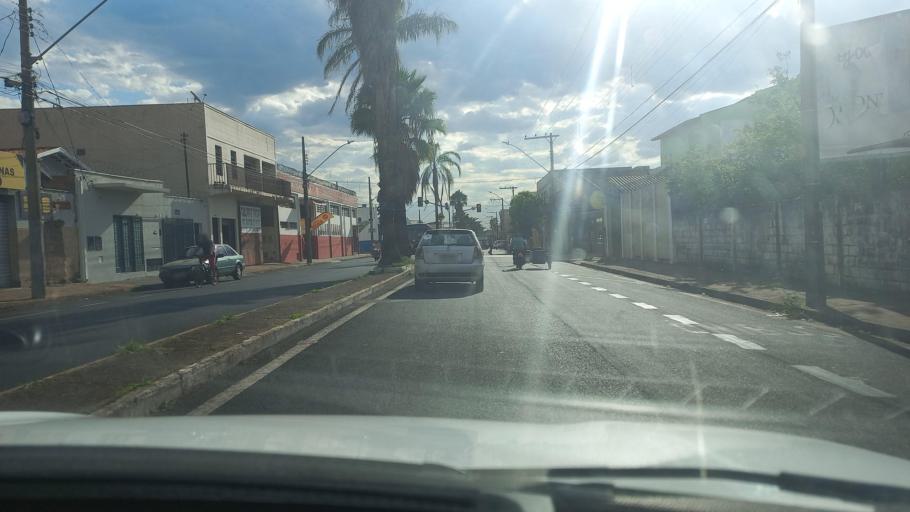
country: BR
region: Minas Gerais
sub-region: Uberaba
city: Uberaba
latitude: -19.7700
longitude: -47.9307
